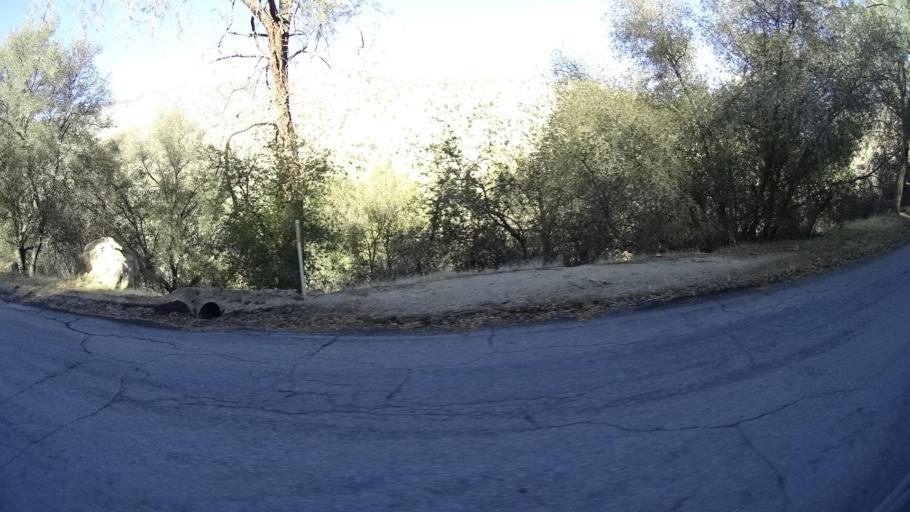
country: US
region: California
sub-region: Kern County
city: Bodfish
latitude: 35.5745
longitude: -118.5457
